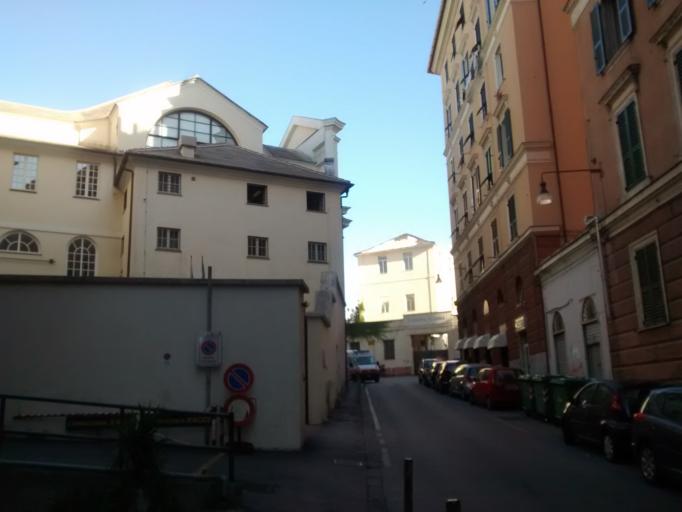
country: IT
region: Liguria
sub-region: Provincia di Genova
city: San Teodoro
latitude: 44.4034
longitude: 8.9382
